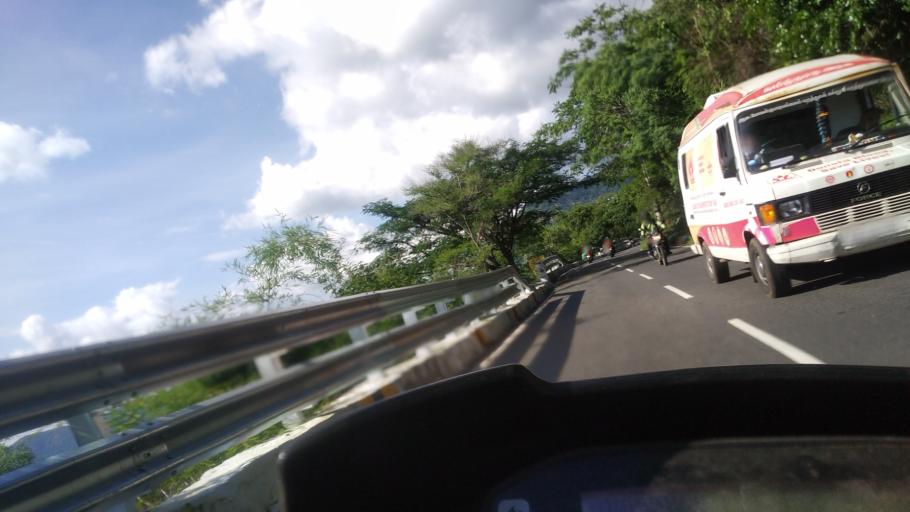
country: IN
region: Tamil Nadu
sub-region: Salem
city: Salem
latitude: 11.7416
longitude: 78.1818
